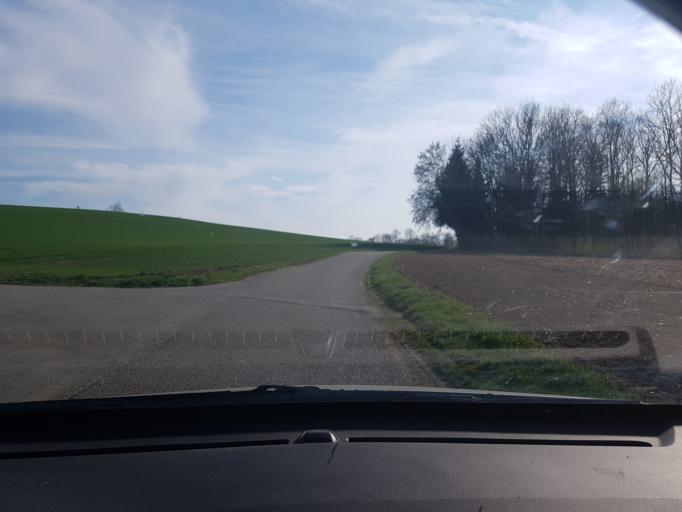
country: AT
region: Upper Austria
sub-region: Politischer Bezirk Linz-Land
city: Ansfelden
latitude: 48.1846
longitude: 14.3322
